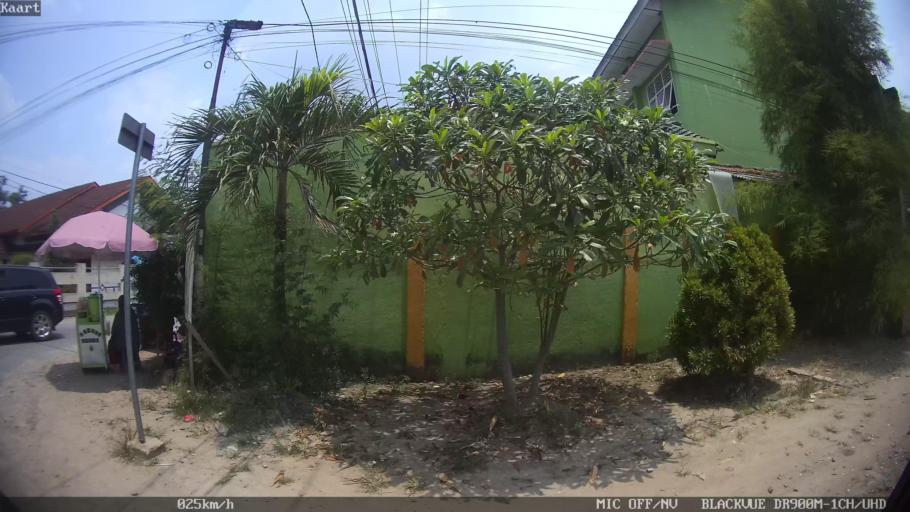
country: ID
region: Lampung
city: Pringsewu
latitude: -5.3507
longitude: 104.9690
